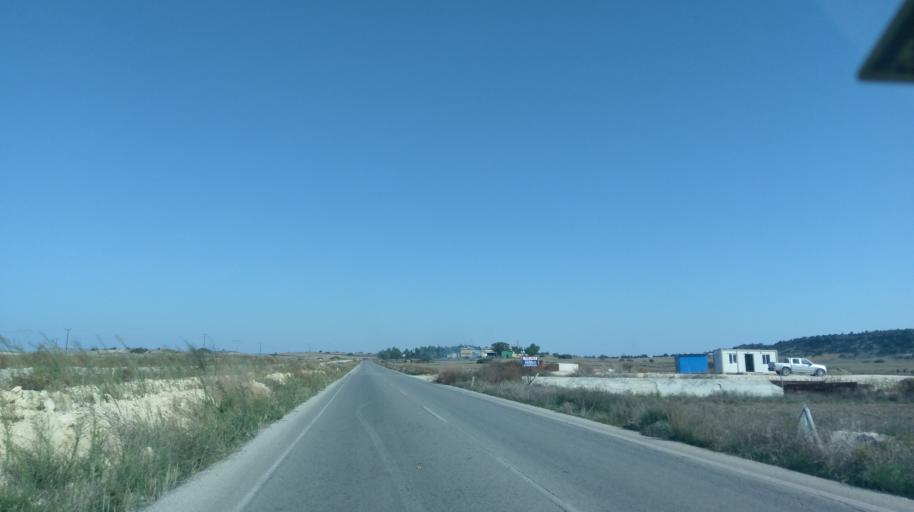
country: CY
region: Ammochostos
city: Trikomo
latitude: 35.3564
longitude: 34.0086
